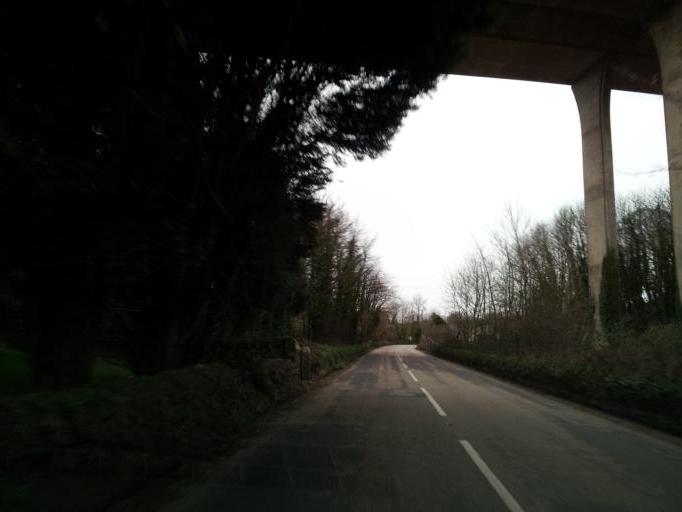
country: GB
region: England
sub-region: Cornwall
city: Redruth
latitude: 50.2410
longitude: -5.2395
